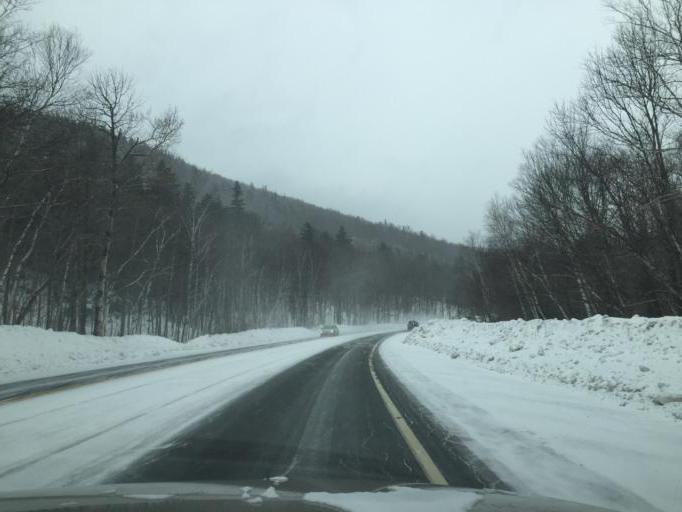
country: US
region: New Hampshire
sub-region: Coos County
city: Gorham
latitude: 44.2324
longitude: -71.2564
